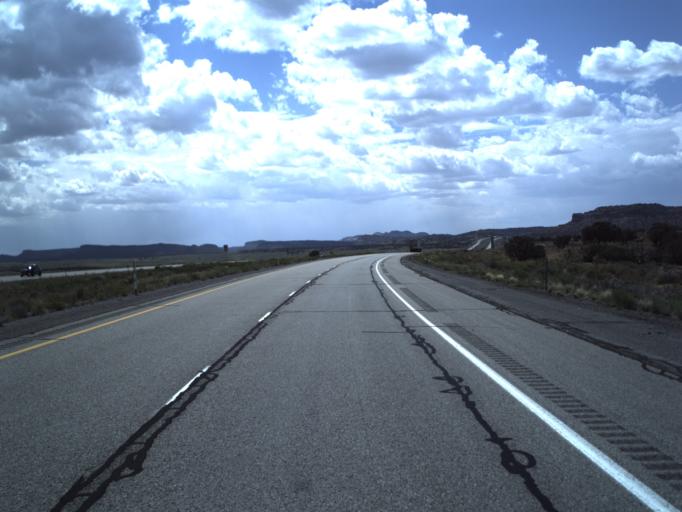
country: US
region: Utah
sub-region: Emery County
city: Castle Dale
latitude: 38.8773
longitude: -110.6656
